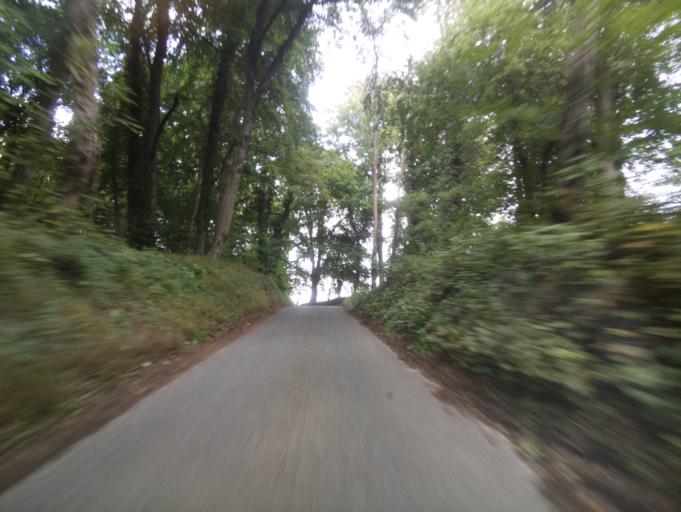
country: GB
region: England
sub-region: Wiltshire
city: Biddestone
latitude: 51.4736
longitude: -2.2245
